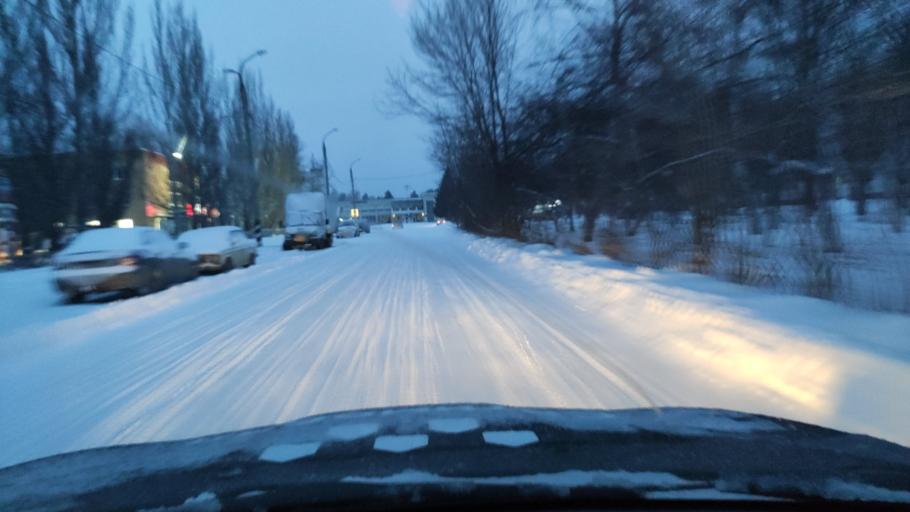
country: RU
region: Samara
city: Povolzhskiy
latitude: 53.5865
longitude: 49.7600
